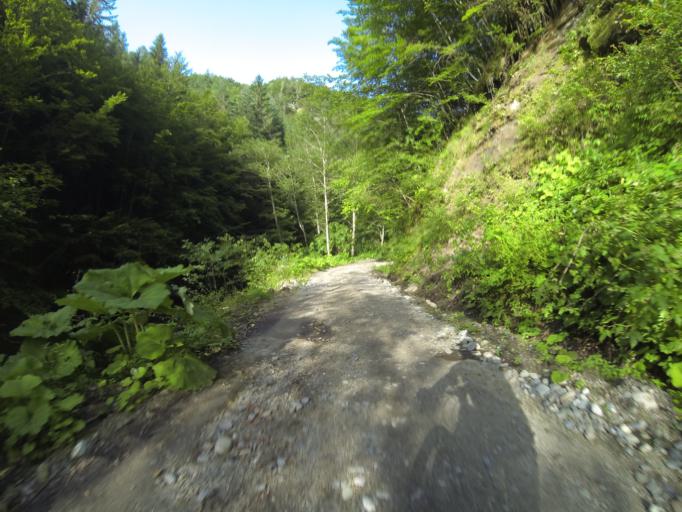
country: RO
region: Valcea
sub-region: Oras Baile Olanesti
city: Baile Olanesti
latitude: 45.2377
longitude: 24.1961
